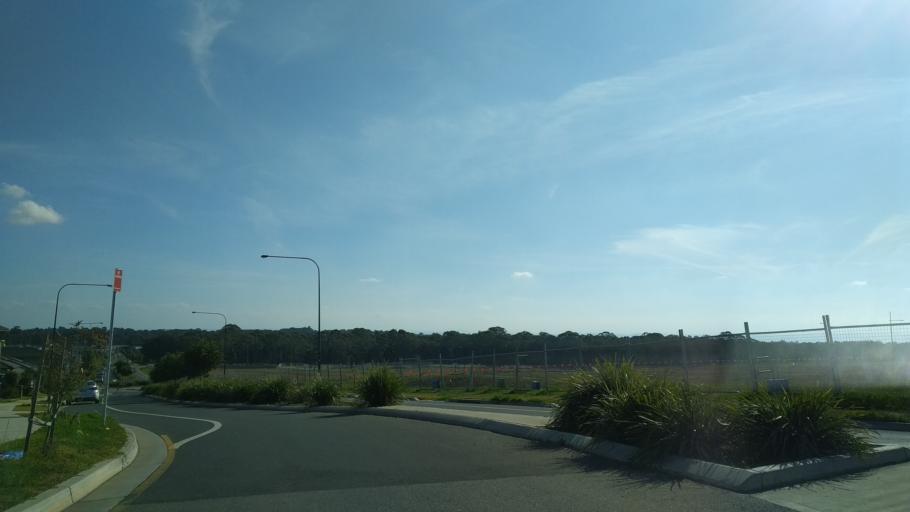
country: AU
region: New South Wales
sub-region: Blacktown
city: Hassall Grove
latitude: -33.7225
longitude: 150.8532
